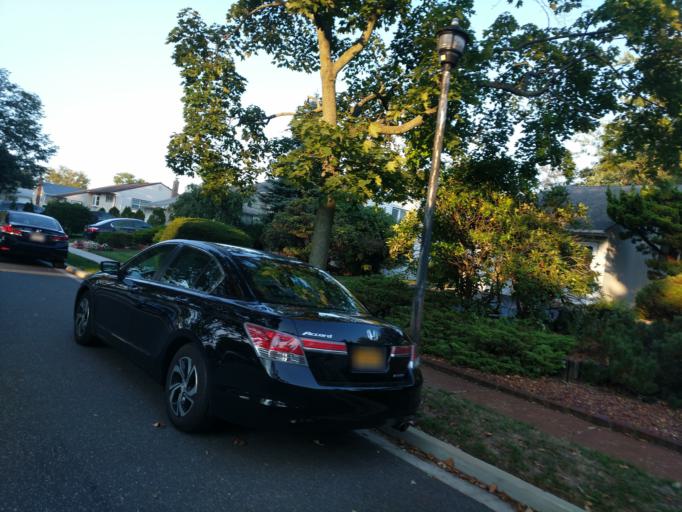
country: US
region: New York
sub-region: Nassau County
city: South Valley Stream
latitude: 40.6573
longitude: -73.7188
